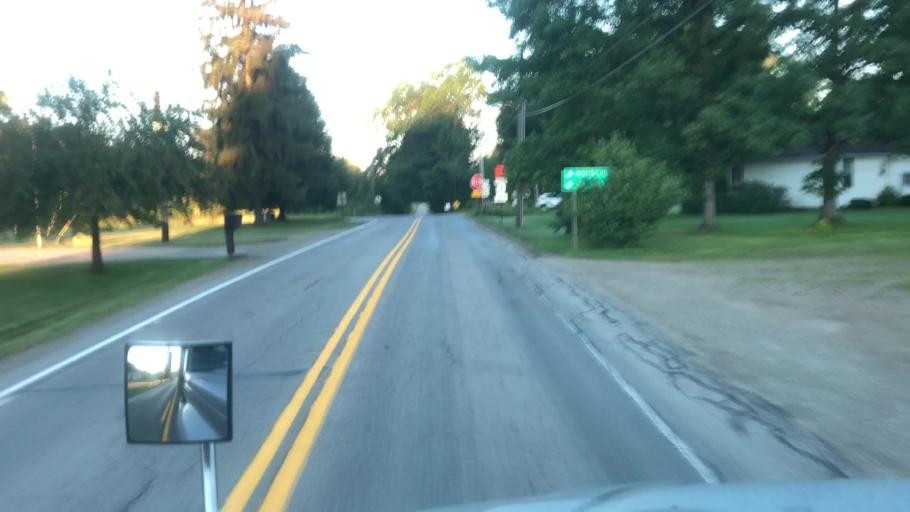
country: US
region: Pennsylvania
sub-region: Crawford County
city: Titusville
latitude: 41.5919
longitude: -79.6090
